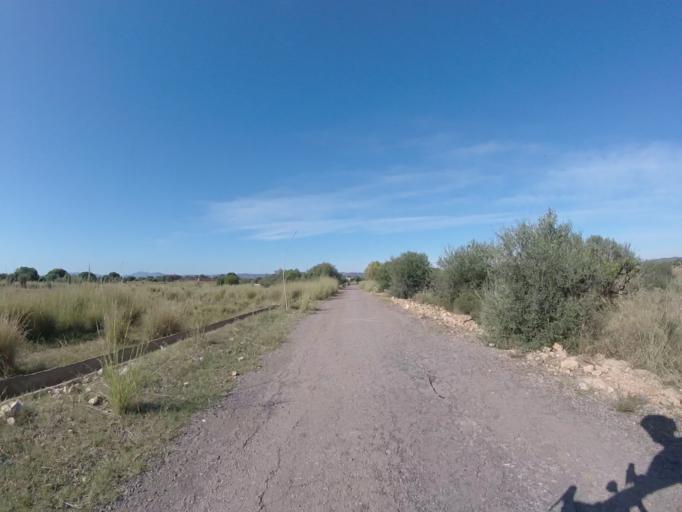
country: ES
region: Valencia
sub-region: Provincia de Castello
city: Torreblanca
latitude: 40.2078
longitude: 0.2439
